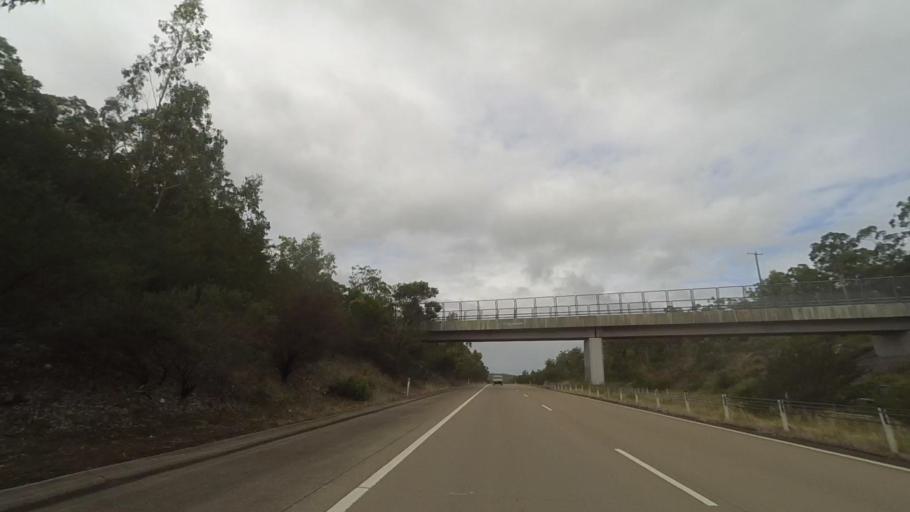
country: AU
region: New South Wales
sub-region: Port Stephens Shire
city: Medowie
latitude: -32.6319
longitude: 151.9389
